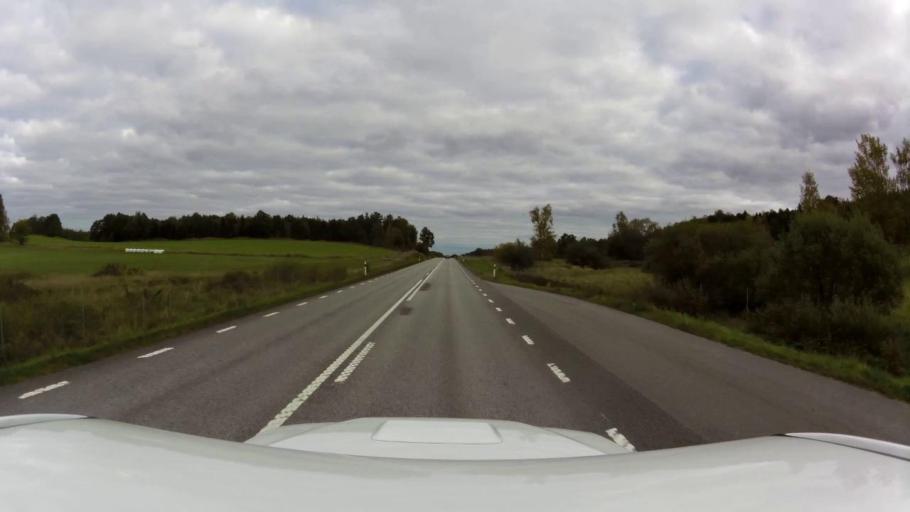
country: SE
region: OEstergoetland
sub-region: Kinda Kommun
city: Rimforsa
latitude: 58.1912
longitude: 15.6666
